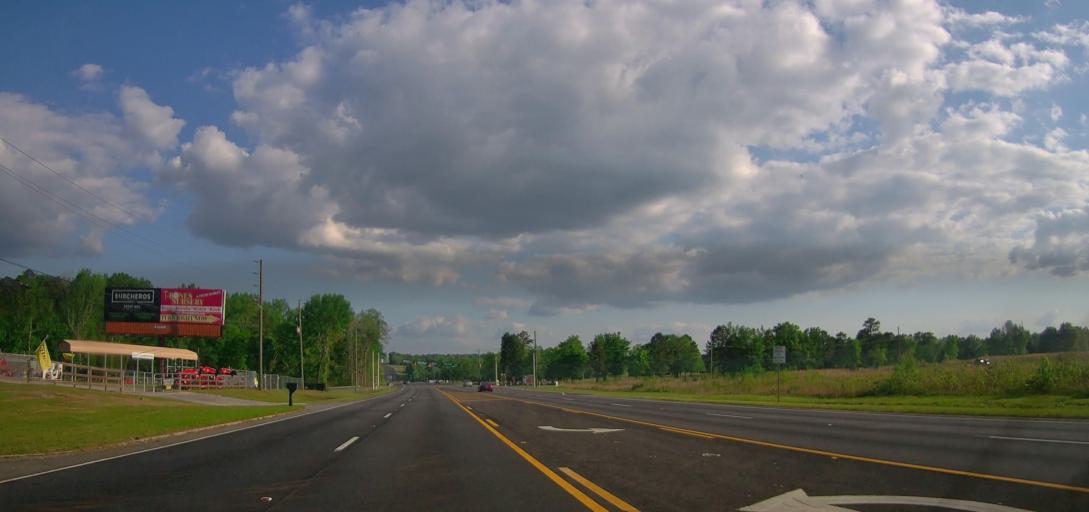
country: US
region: Georgia
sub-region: Baldwin County
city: Milledgeville
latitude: 33.1679
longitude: -83.2806
